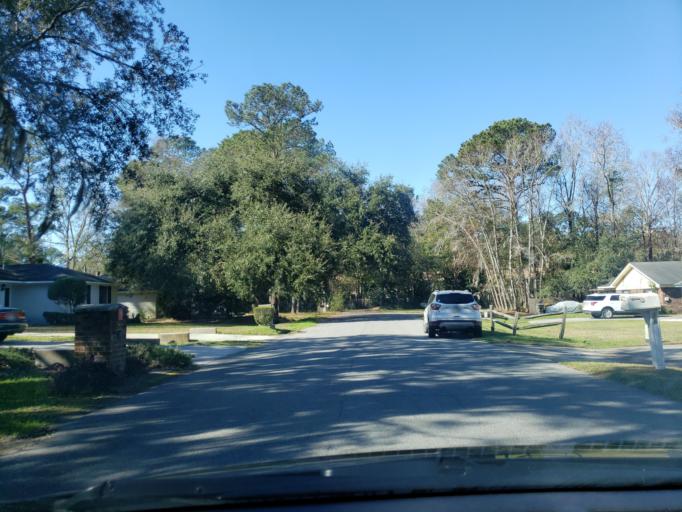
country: US
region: Georgia
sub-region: Chatham County
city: Montgomery
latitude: 31.9758
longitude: -81.1360
